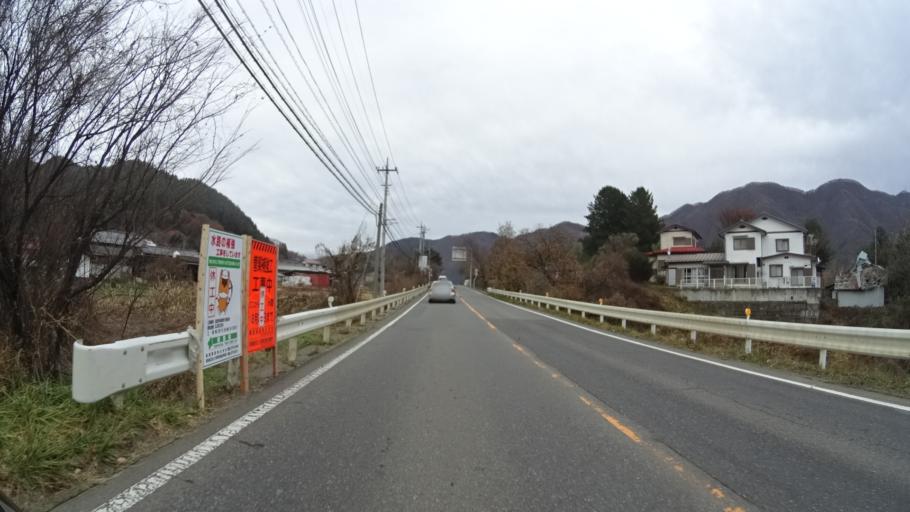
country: JP
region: Gunma
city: Numata
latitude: 36.6722
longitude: 139.1973
